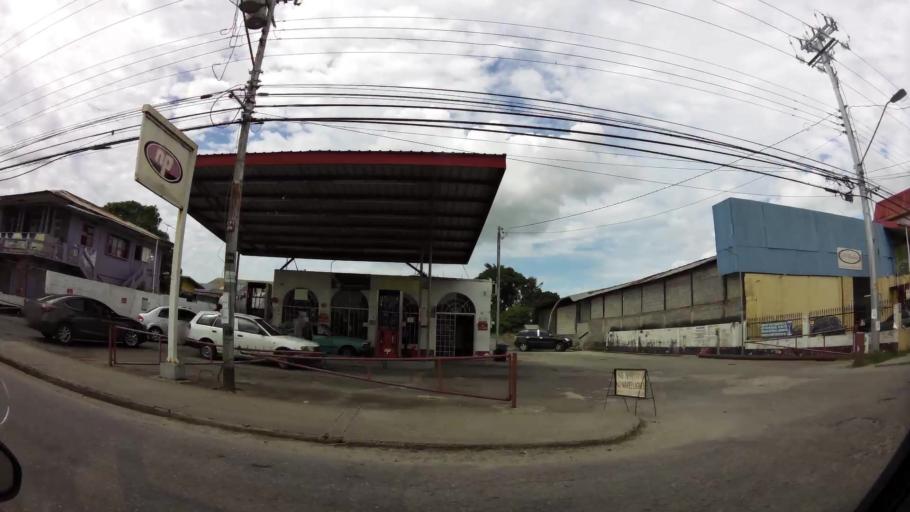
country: TT
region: Couva-Tabaquite-Talparo
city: Couva
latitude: 10.4056
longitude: -61.4719
